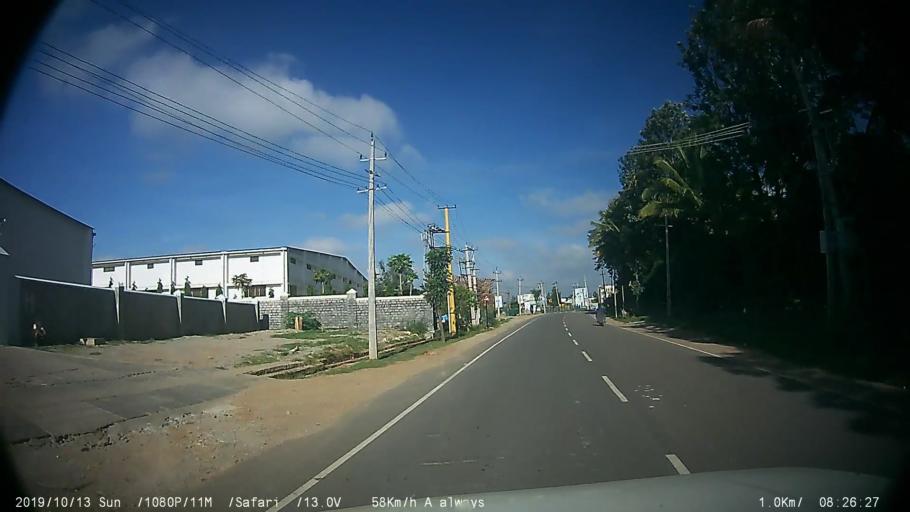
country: IN
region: Karnataka
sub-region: Bangalore Urban
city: Anekal
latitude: 12.8202
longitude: 77.6235
